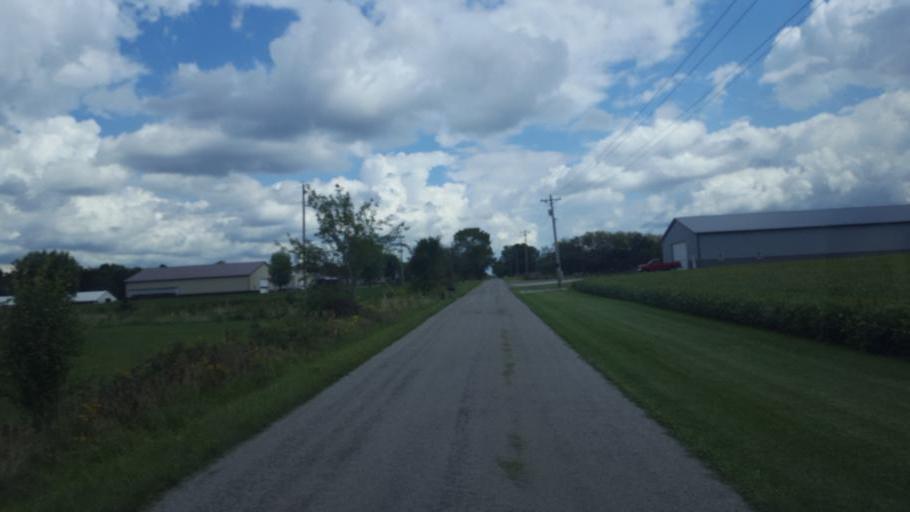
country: US
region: Ohio
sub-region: Huron County
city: Plymouth
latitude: 41.0453
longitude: -82.6175
